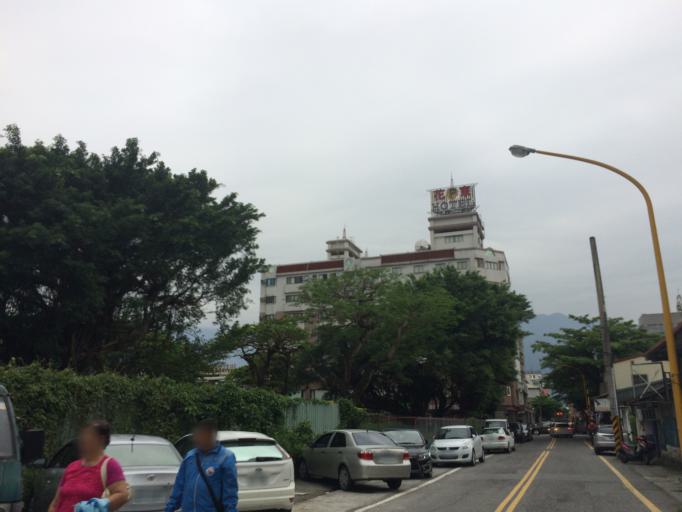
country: TW
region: Taiwan
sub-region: Hualien
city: Hualian
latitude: 23.9802
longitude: 121.6089
